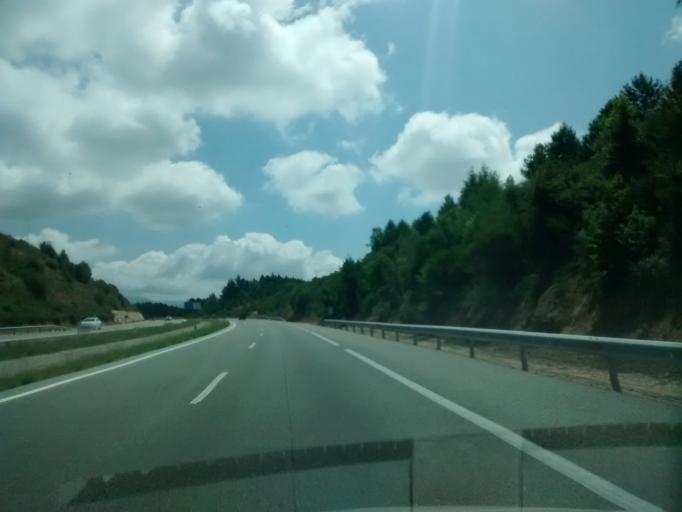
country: ES
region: Castille and Leon
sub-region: Provincia de Leon
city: Ponferrada
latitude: 42.5614
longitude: -6.5666
